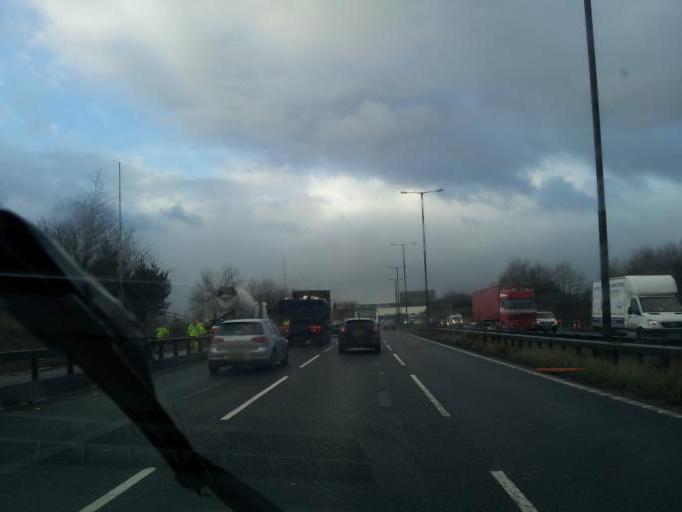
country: GB
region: England
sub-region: Manchester
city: Heywood
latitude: 53.5722
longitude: -2.2171
